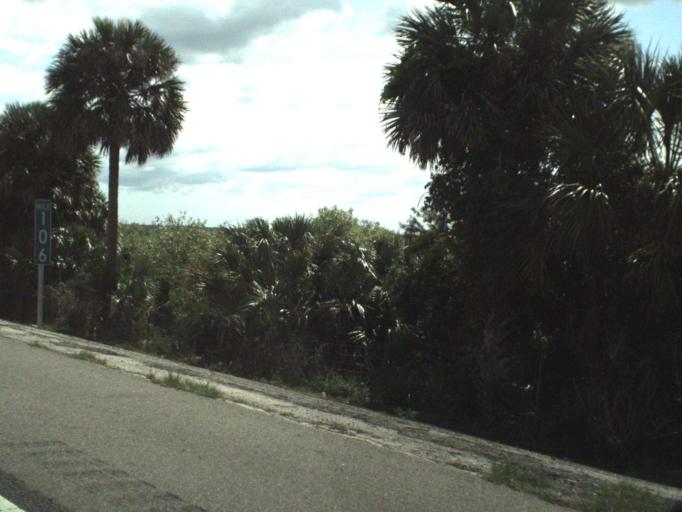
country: US
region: Florida
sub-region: Volusia County
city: DeBary
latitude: 28.8514
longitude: -81.3031
